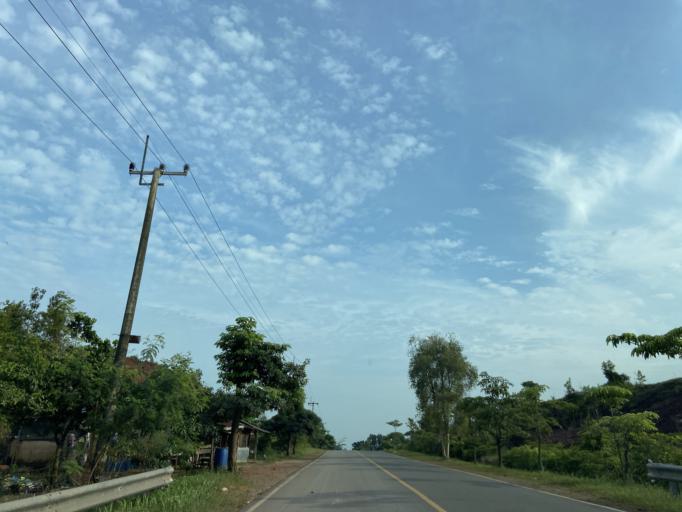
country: ID
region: Riau Islands
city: Tanjungpinang
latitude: 0.9147
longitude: 104.1206
